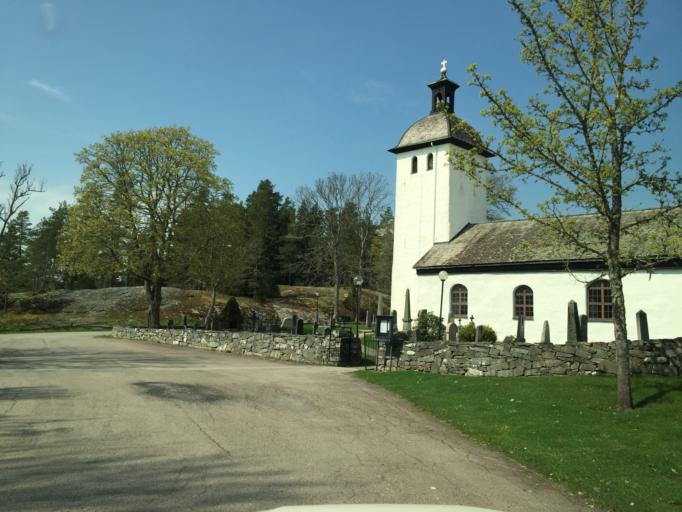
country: SE
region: Vaestra Goetaland
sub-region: Bengtsfors Kommun
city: Billingsfors
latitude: 58.9333
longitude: 12.2076
